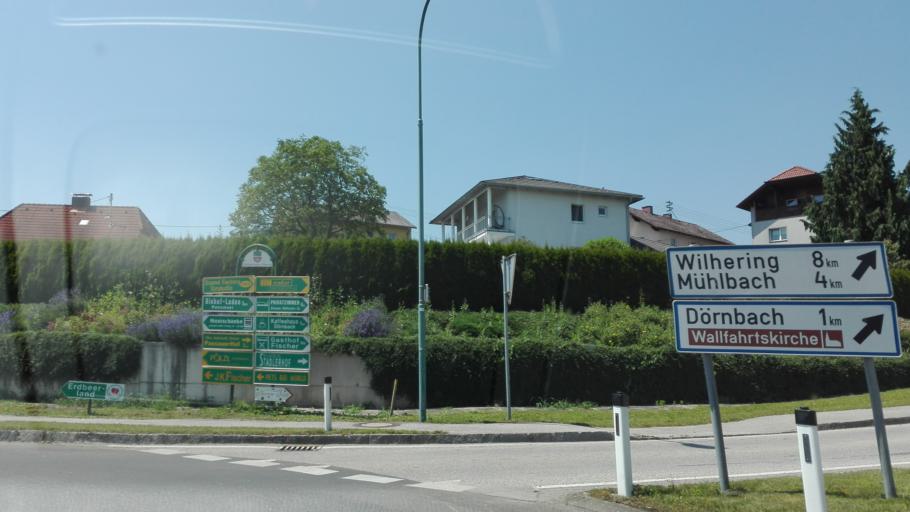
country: AT
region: Upper Austria
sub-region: Politischer Bezirk Linz-Land
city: Pasching
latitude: 48.2724
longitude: 14.2003
